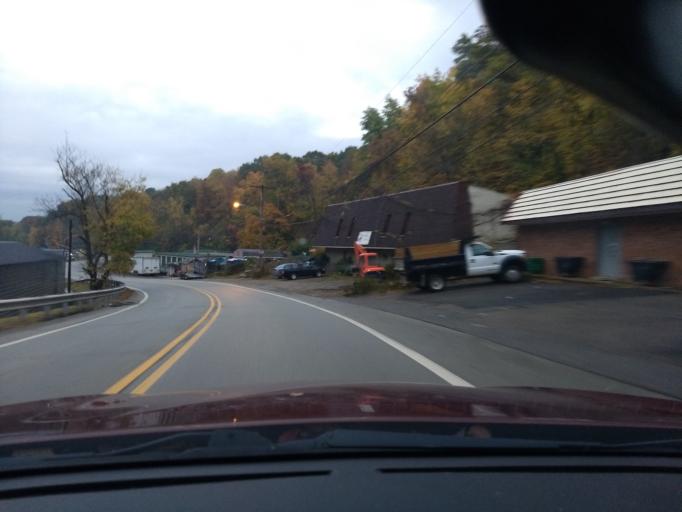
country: US
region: Pennsylvania
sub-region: Allegheny County
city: Pleasant Hills
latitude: 40.3522
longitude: -79.9589
